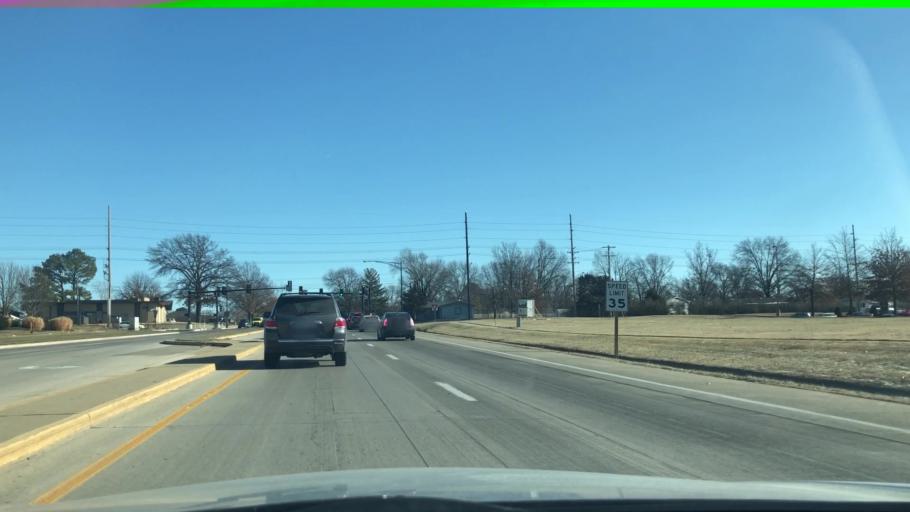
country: US
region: Missouri
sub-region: Boone County
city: Columbia
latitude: 38.9548
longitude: -92.3824
